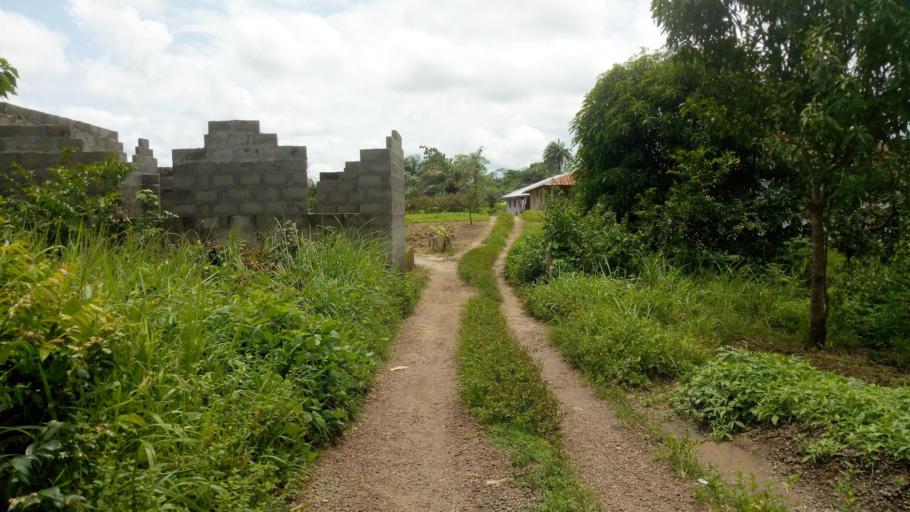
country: SL
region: Northern Province
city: Magburaka
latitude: 8.7197
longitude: -11.9598
